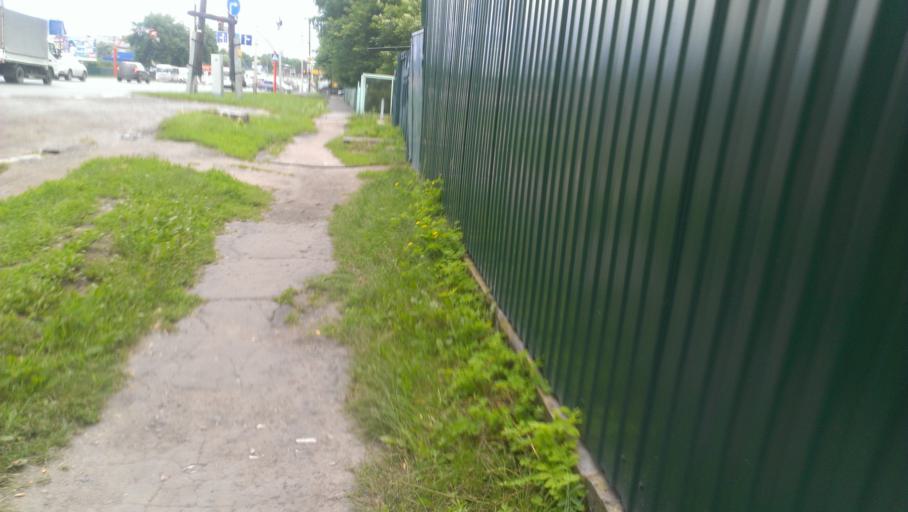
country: RU
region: Altai Krai
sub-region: Gorod Barnaulskiy
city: Barnaul
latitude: 53.3396
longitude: 83.7308
